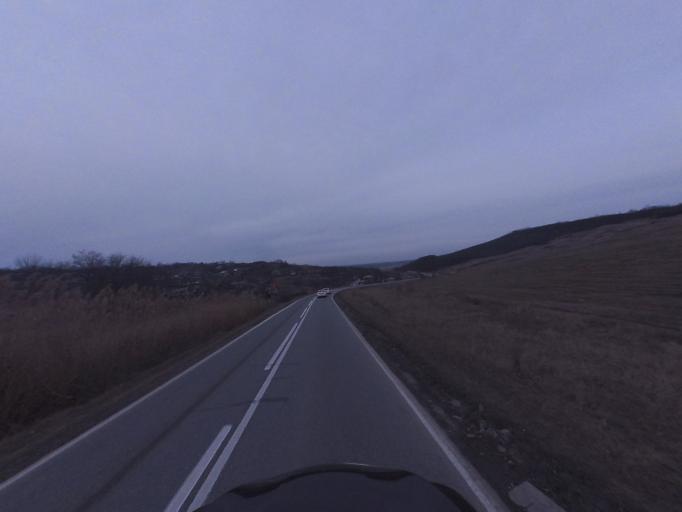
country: RO
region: Iasi
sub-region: Comuna Popricani
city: Popricani
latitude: 47.2941
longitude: 27.5101
